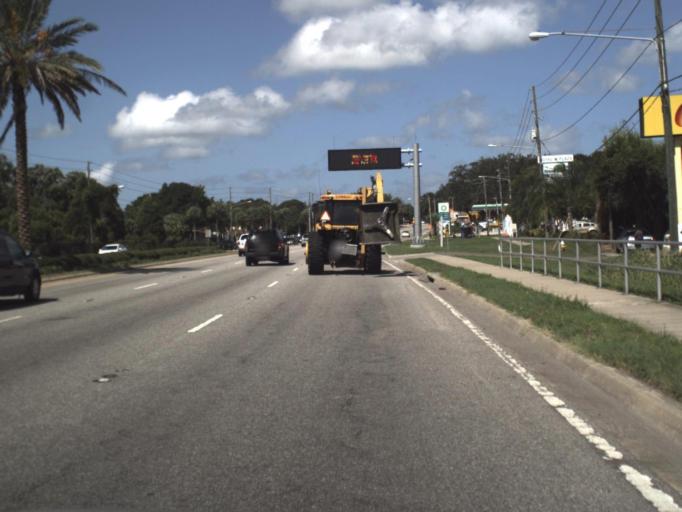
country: US
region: Florida
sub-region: Pinellas County
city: Largo
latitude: 27.9168
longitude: -82.7772
